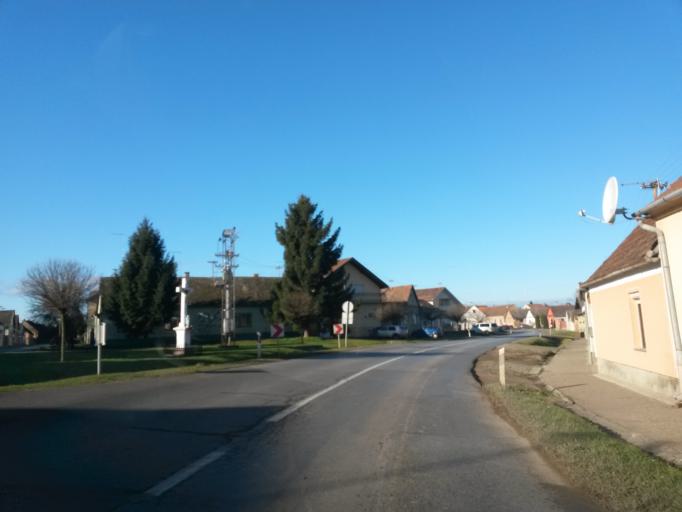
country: HR
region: Osjecko-Baranjska
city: Petrijevci
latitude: 45.6131
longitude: 18.5411
